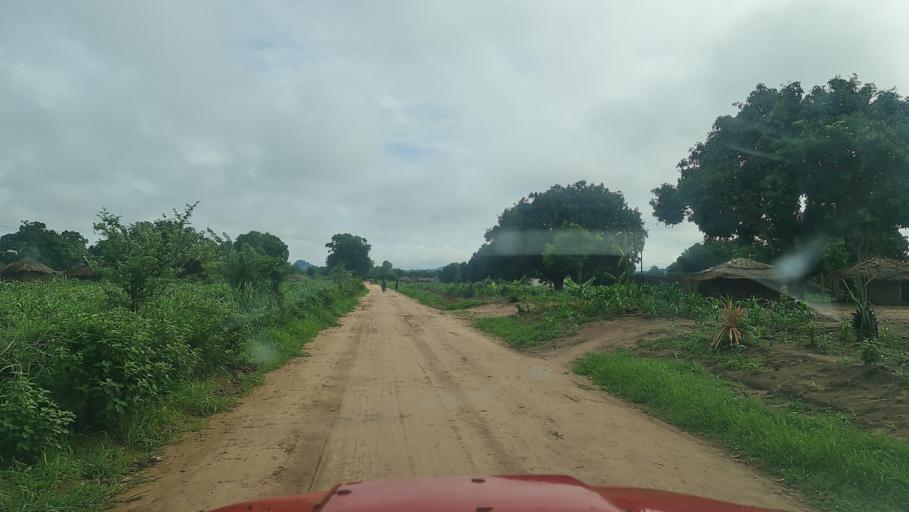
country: MW
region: Southern Region
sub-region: Nsanje District
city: Nsanje
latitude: -17.2885
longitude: 35.6052
